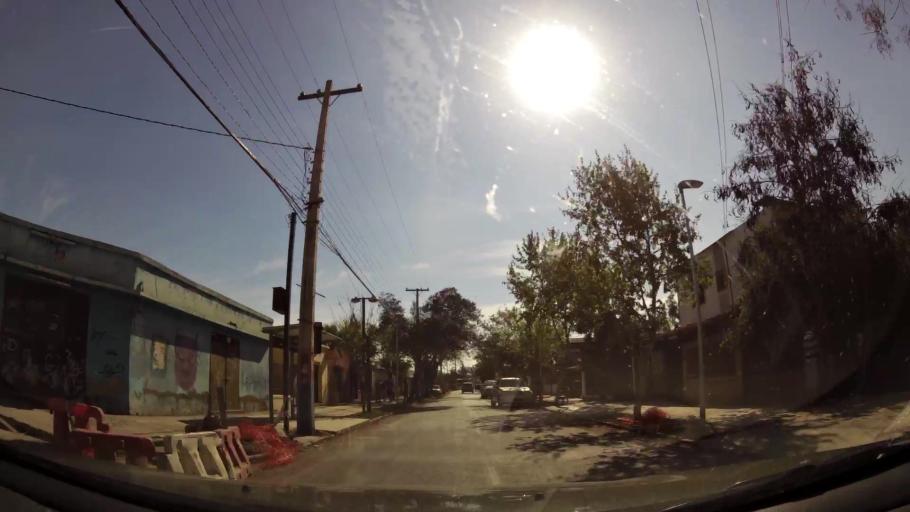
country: CL
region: Santiago Metropolitan
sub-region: Provincia de Santiago
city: Santiago
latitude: -33.4094
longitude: -70.6316
